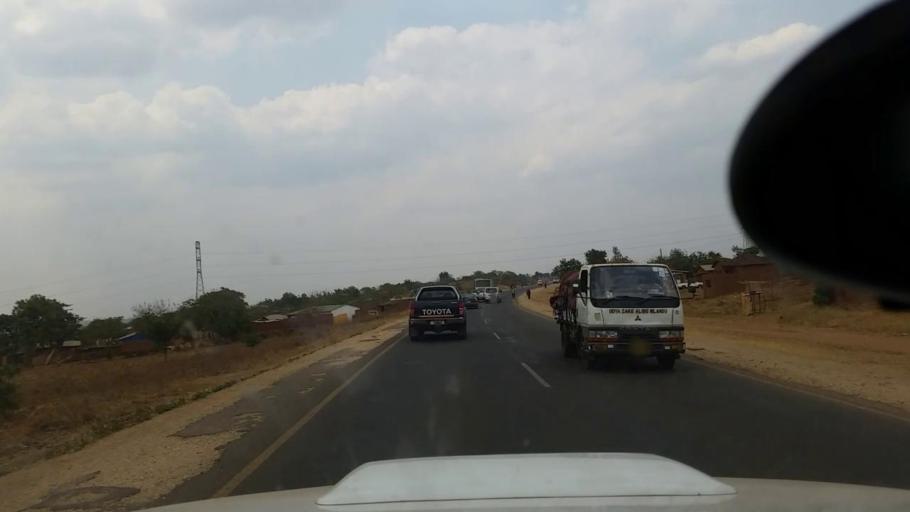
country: MW
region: Central Region
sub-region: Lilongwe District
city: Lilongwe
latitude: -13.8673
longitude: 33.8288
